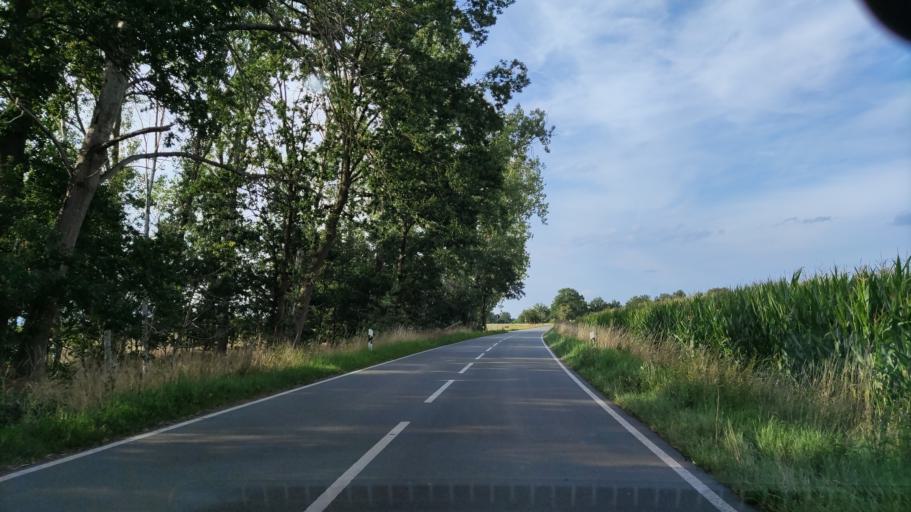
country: DE
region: Lower Saxony
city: Dannenberg
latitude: 53.1149
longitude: 11.1128
